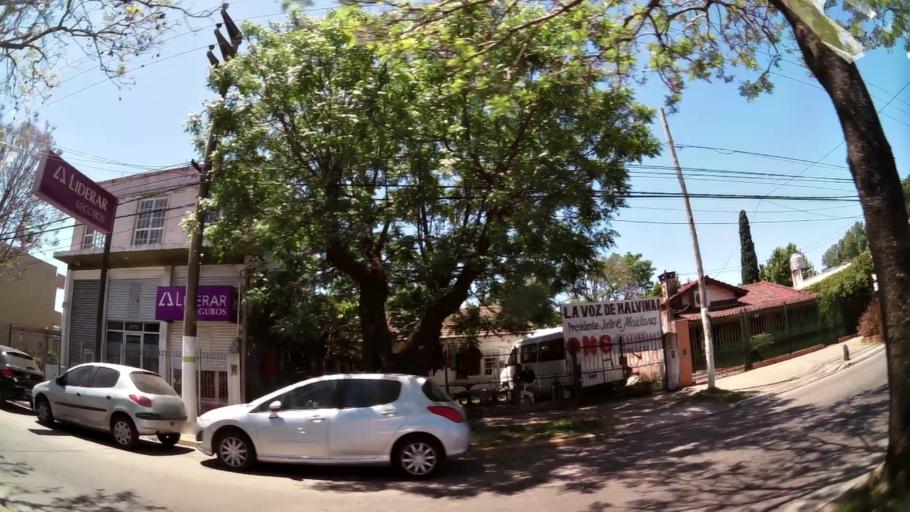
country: AR
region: Buenos Aires
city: Hurlingham
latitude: -34.5033
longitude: -58.6891
